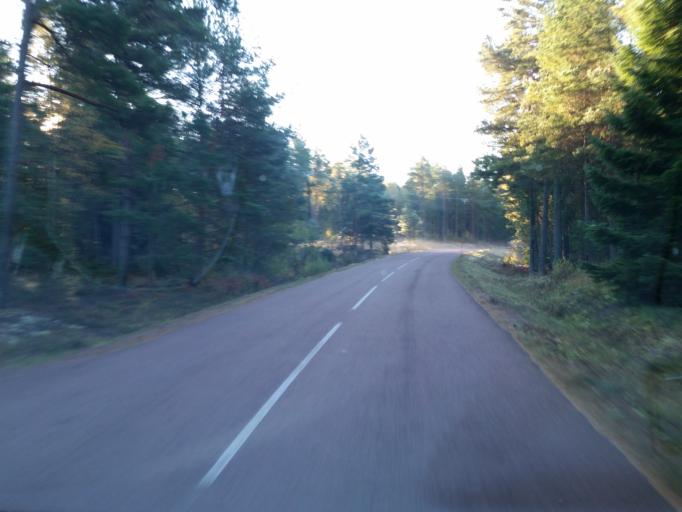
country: AX
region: Alands skaergard
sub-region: Vardoe
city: Vardoe
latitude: 60.2886
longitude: 20.3910
